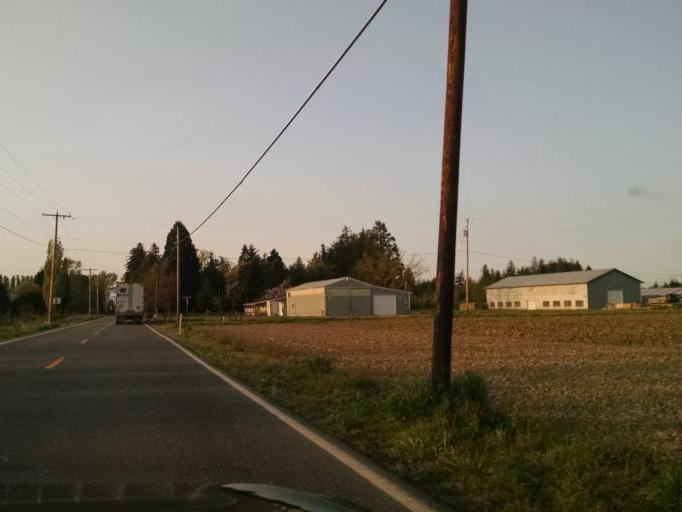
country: US
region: Washington
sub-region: Whatcom County
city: Nooksack
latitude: 48.9121
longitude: -122.3208
